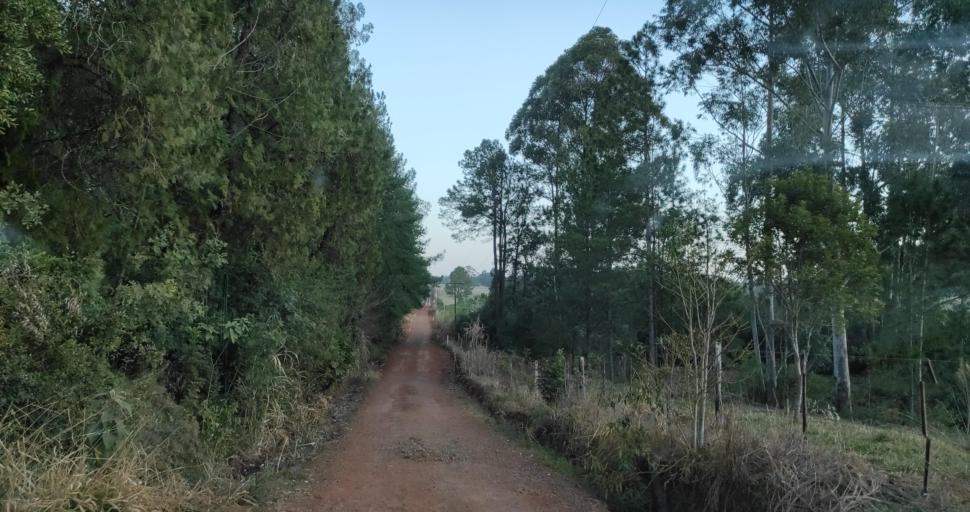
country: AR
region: Misiones
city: Capiovi
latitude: -26.8961
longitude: -55.0496
